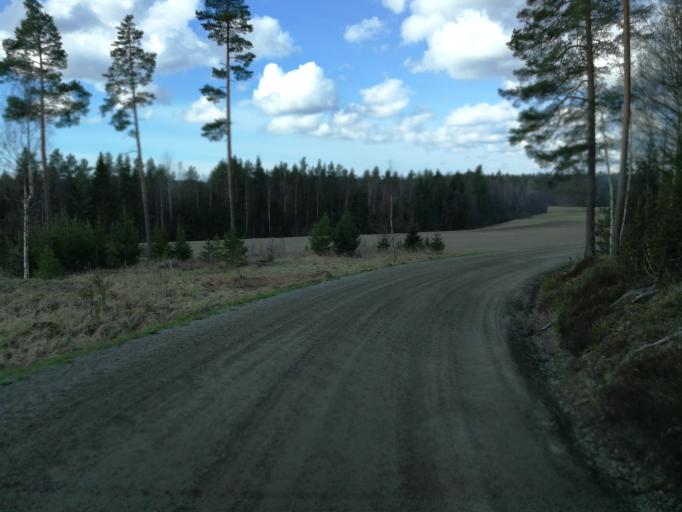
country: FI
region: Uusimaa
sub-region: Raaseporin
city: Inga
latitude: 60.1190
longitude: 24.0435
